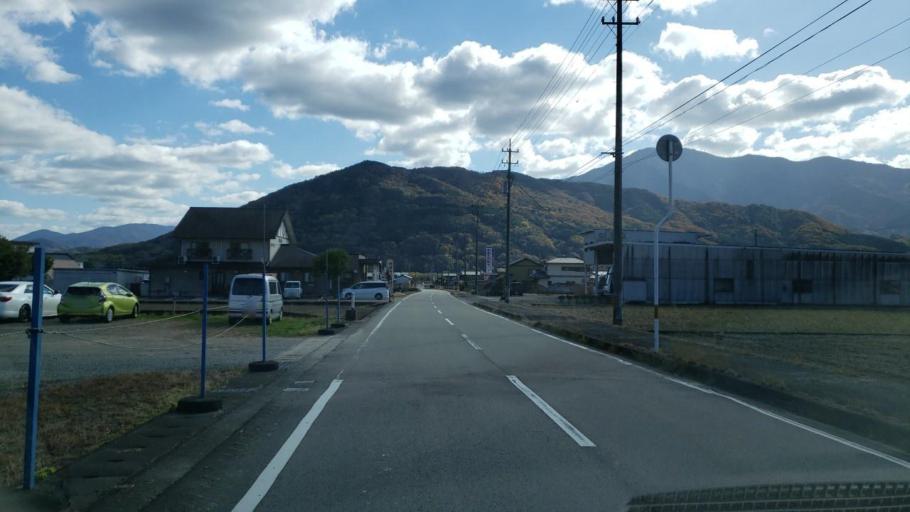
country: JP
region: Tokushima
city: Wakimachi
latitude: 34.0709
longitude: 134.1794
